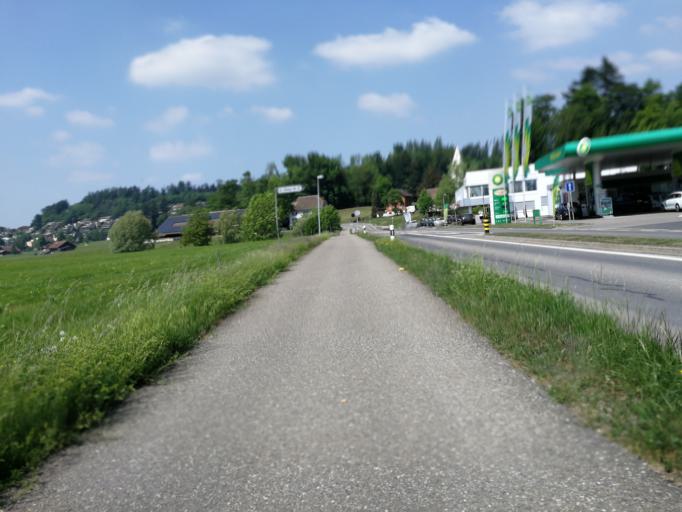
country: CH
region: Saint Gallen
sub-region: Wahlkreis See-Gaster
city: Jona
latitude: 47.2255
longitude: 8.8620
